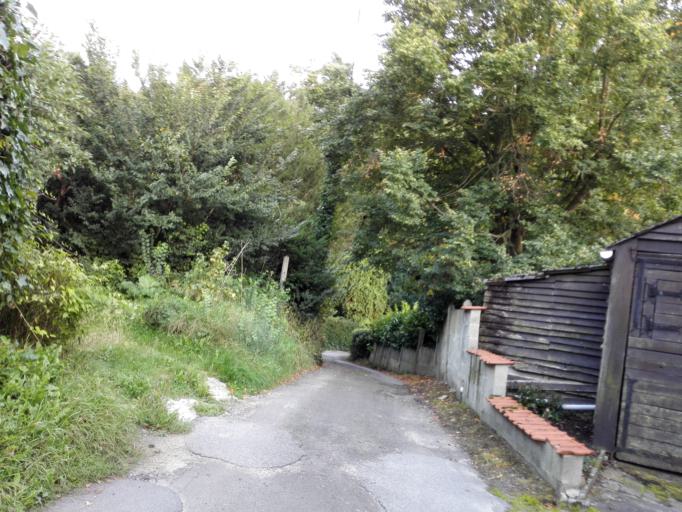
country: BE
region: Flanders
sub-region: Provincie Vlaams-Brabant
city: Oud-Heverlee
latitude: 50.8031
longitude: 4.6540
